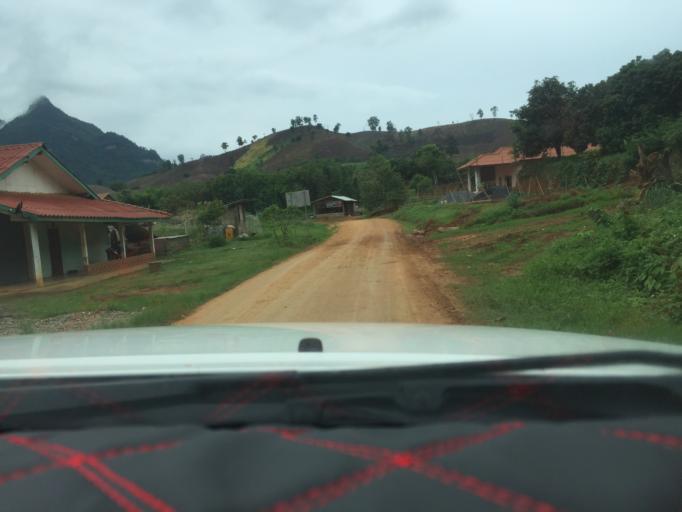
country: TH
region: Phayao
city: Phu Sang
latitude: 19.7653
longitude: 100.5068
